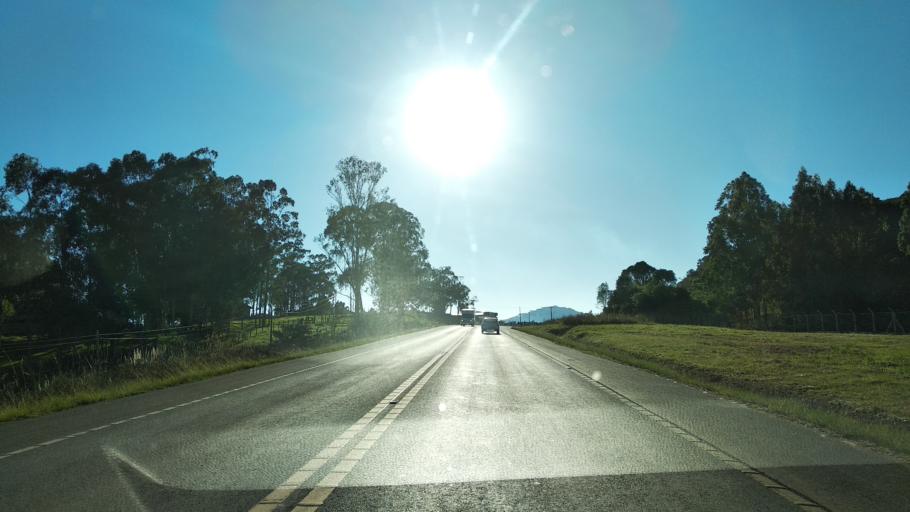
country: BR
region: Santa Catarina
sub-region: Lages
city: Lages
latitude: -27.7931
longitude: -50.3762
